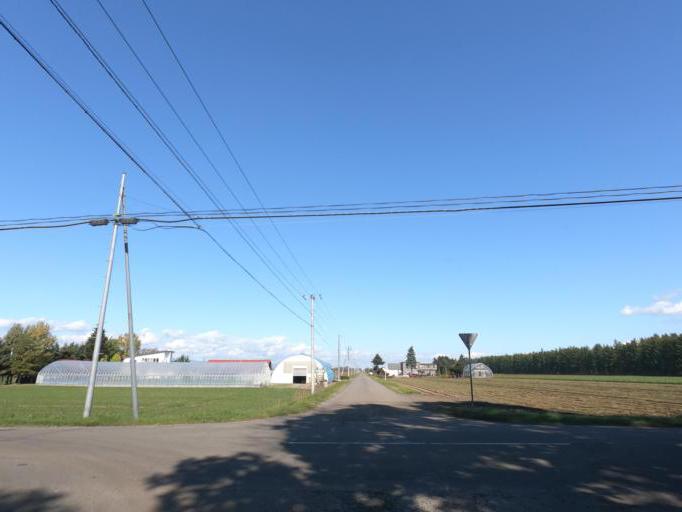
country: JP
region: Hokkaido
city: Otofuke
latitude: 43.0766
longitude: 143.2599
